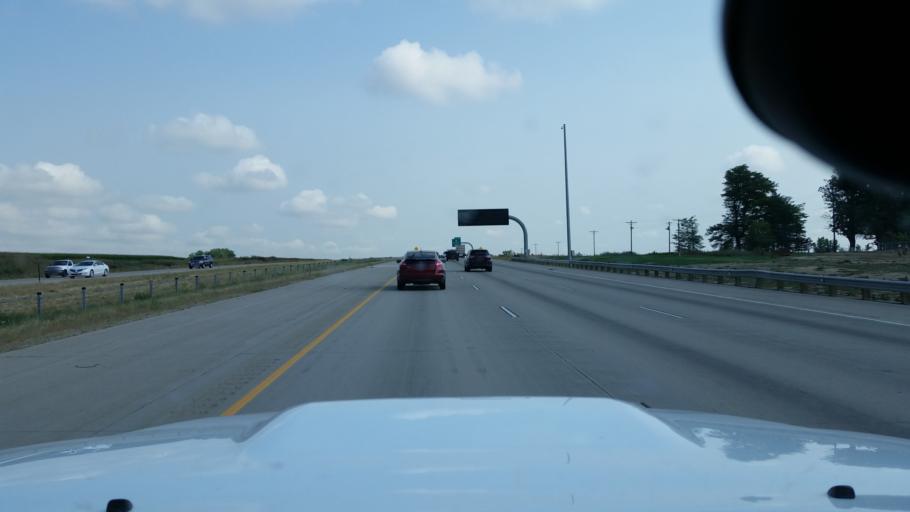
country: US
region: Colorado
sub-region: Weld County
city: Mead
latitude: 40.1824
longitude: -104.9800
